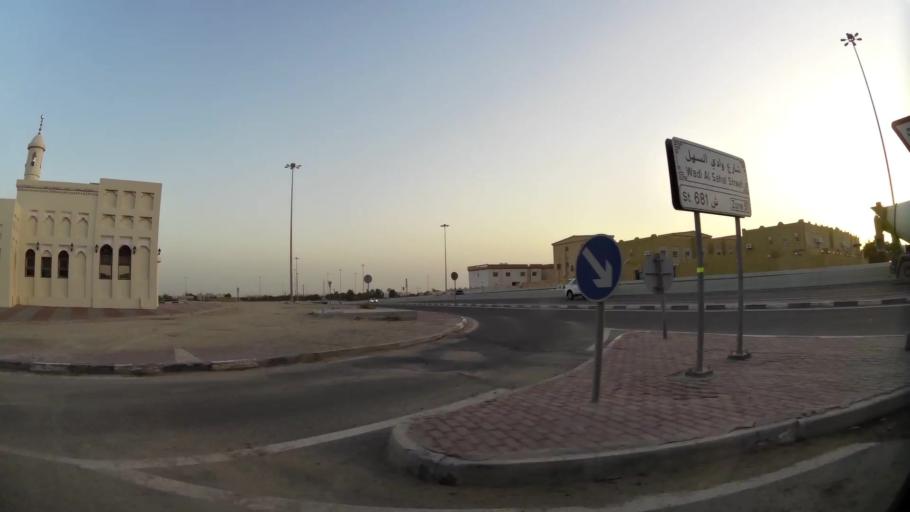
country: QA
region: Baladiyat ar Rayyan
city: Ar Rayyan
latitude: 25.3242
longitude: 51.4611
